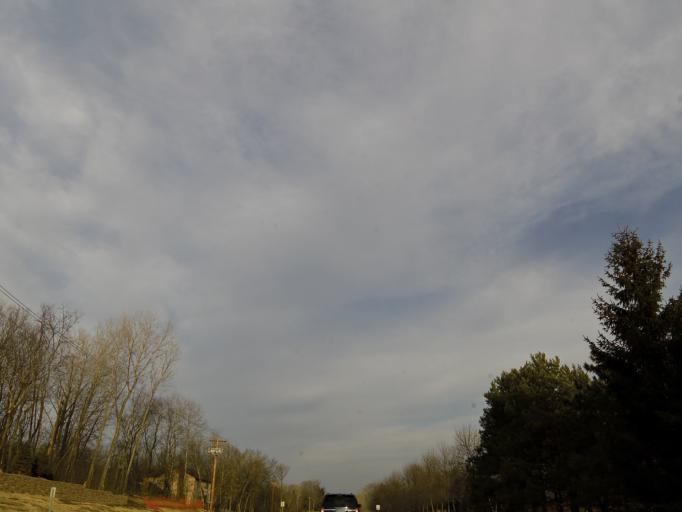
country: US
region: Minnesota
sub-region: Dakota County
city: Lakeville
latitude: 44.6813
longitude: -93.2727
